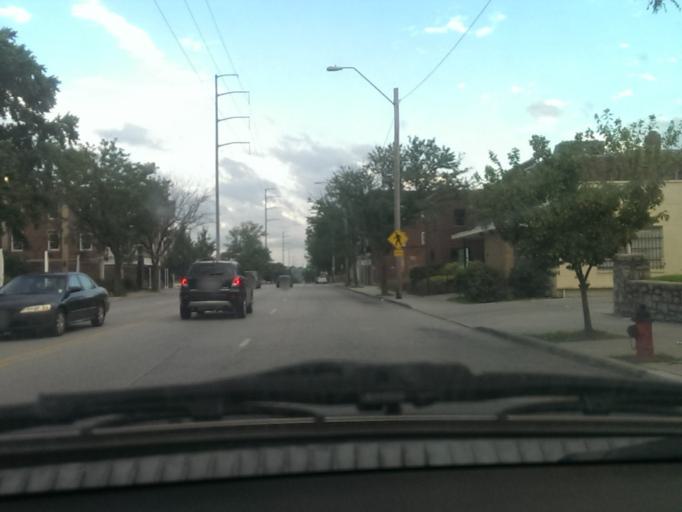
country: US
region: Missouri
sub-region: Jackson County
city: Kansas City
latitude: 39.0553
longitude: -94.5723
